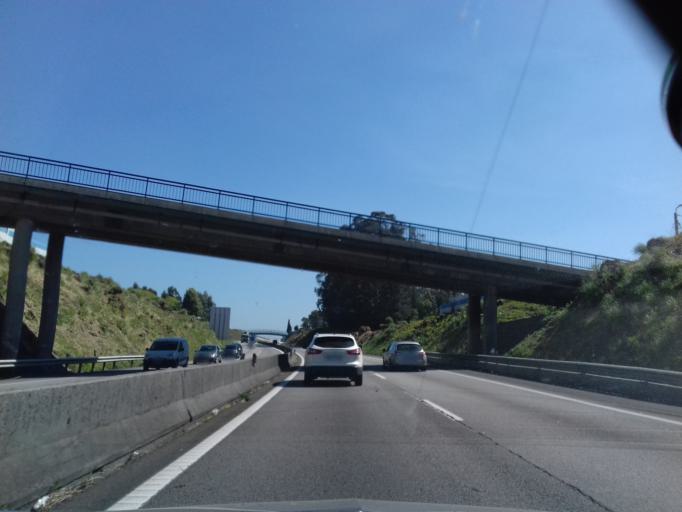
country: PT
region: Porto
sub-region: Vila Nova de Gaia
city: Arcozelo
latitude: 41.0571
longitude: -8.6400
